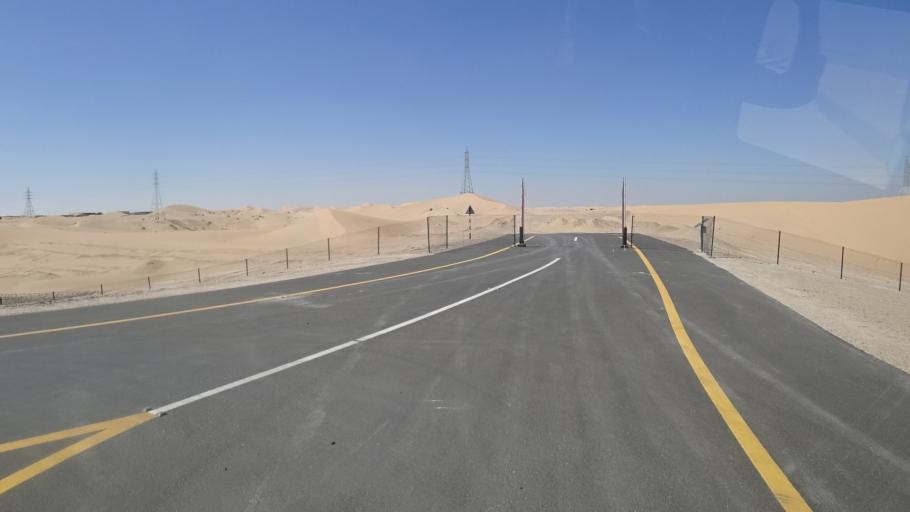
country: AE
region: Abu Dhabi
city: Abu Dhabi
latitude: 24.1218
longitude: 54.8346
